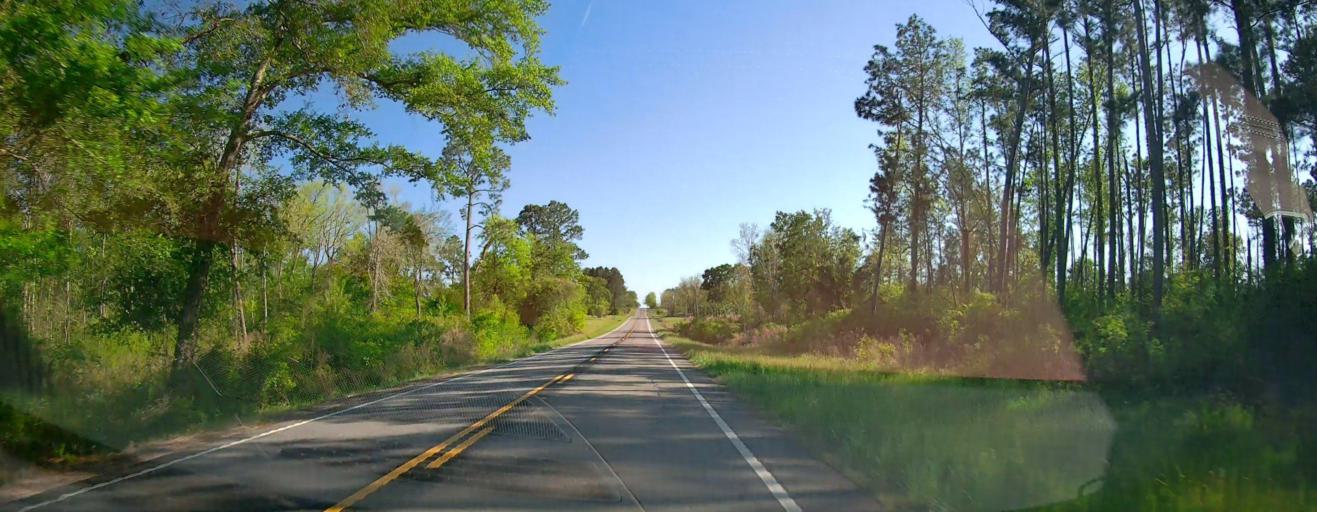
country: US
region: Georgia
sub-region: Wilcox County
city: Rochelle
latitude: 31.8324
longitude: -83.4890
